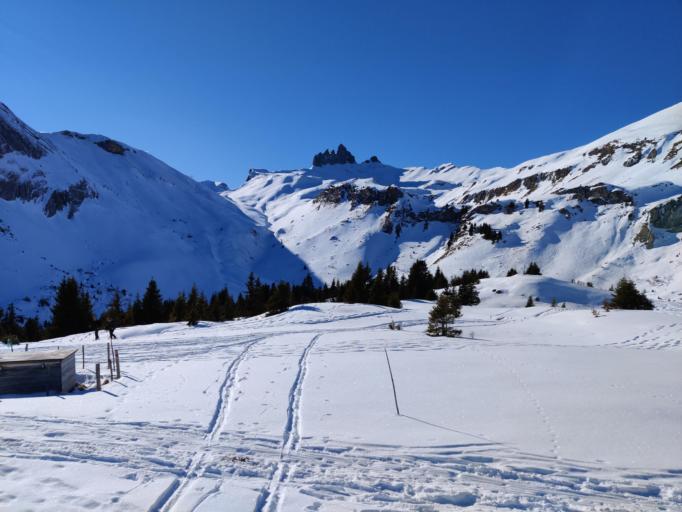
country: CH
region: Bern
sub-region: Interlaken-Oberhasli District
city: Lauterbrunnen
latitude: 46.6186
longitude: 7.8685
